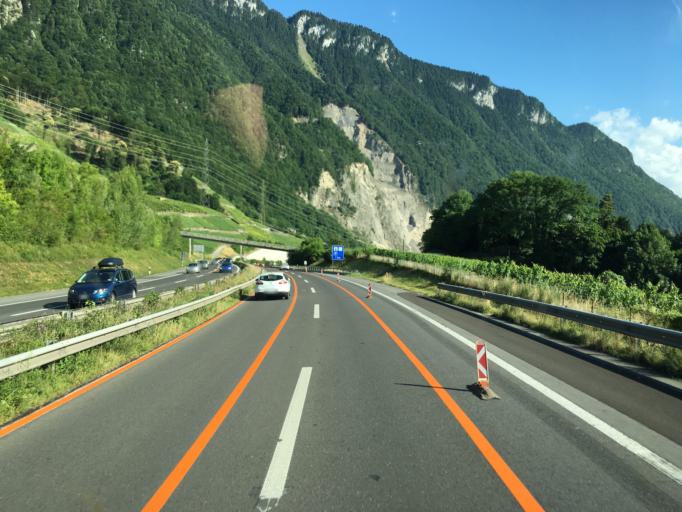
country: CH
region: Vaud
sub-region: Aigle District
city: Villeneuve
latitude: 46.3996
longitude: 6.9342
